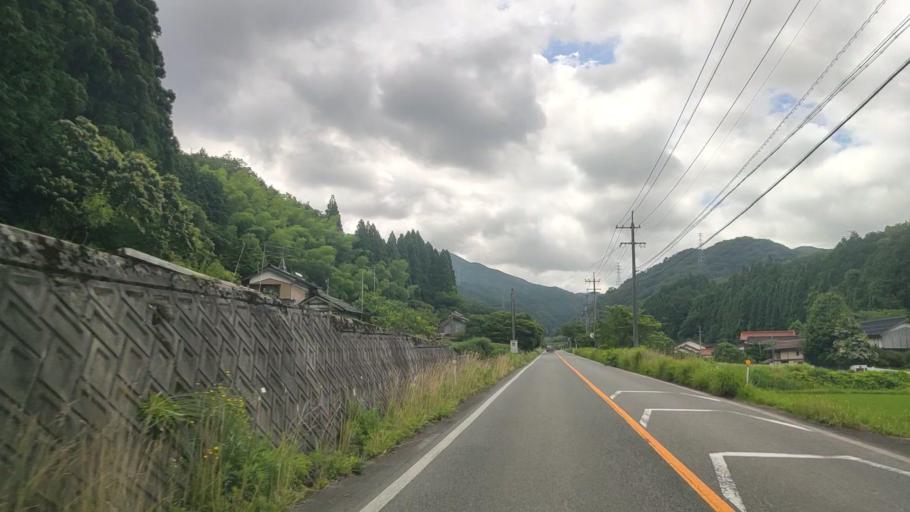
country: JP
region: Tottori
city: Yonago
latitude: 35.2930
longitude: 133.4199
